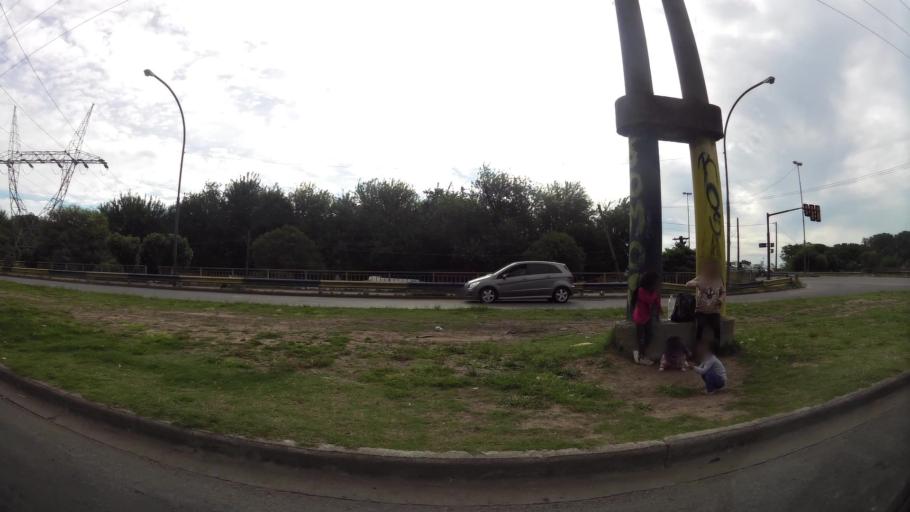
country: AR
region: Santa Fe
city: Gobernador Galvez
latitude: -32.9923
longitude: -60.6888
